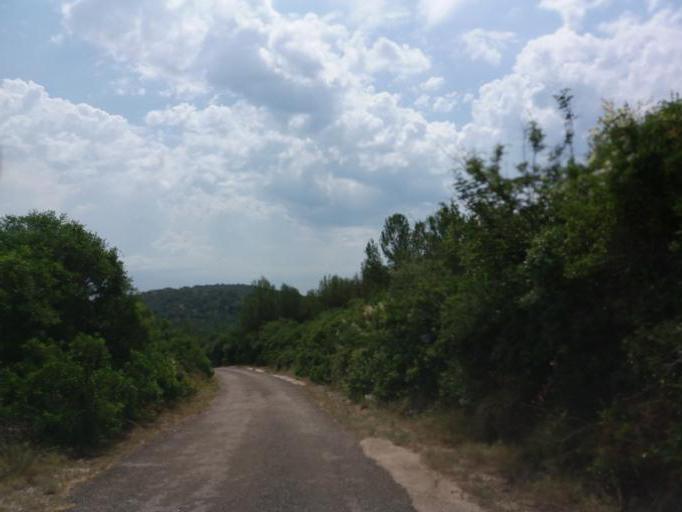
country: HR
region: Zadarska
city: Sali
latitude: 43.9165
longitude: 15.1273
